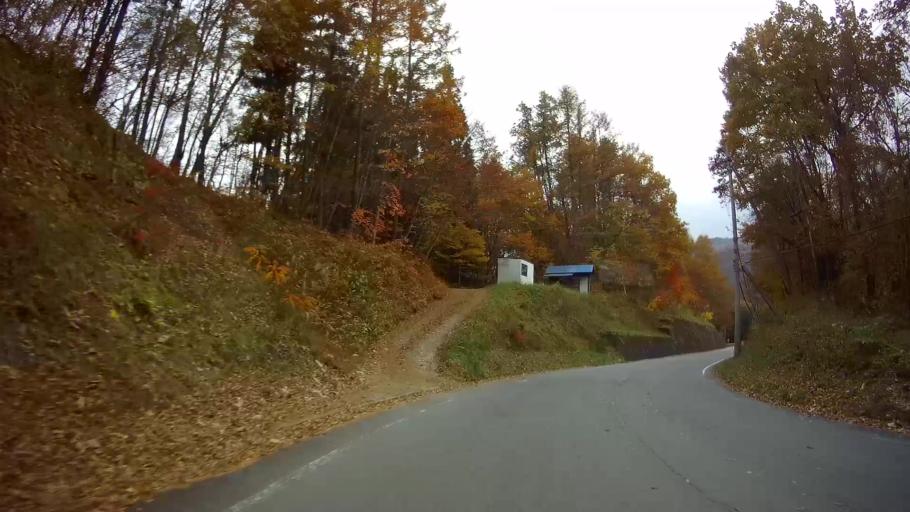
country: JP
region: Gunma
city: Nakanojomachi
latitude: 36.6543
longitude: 138.6532
